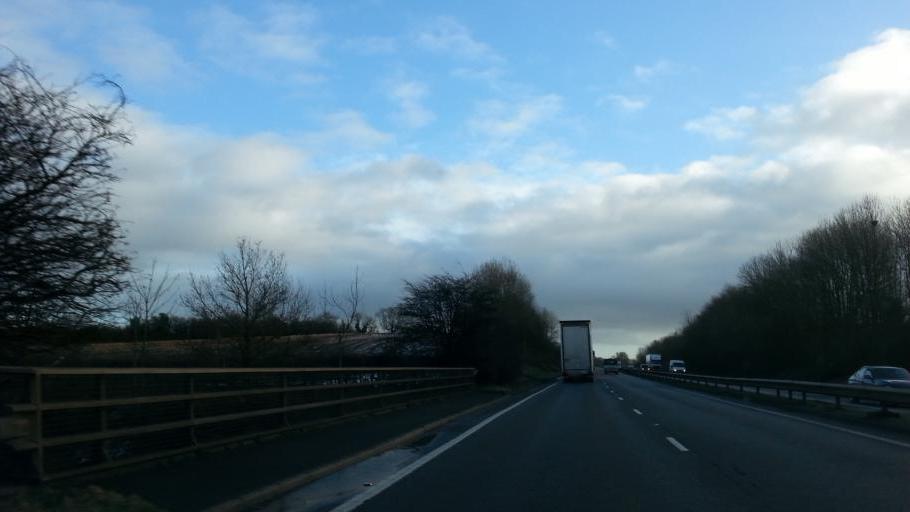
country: GB
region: England
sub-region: Staffordshire
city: Cheadle
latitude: 52.9500
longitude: -2.0161
